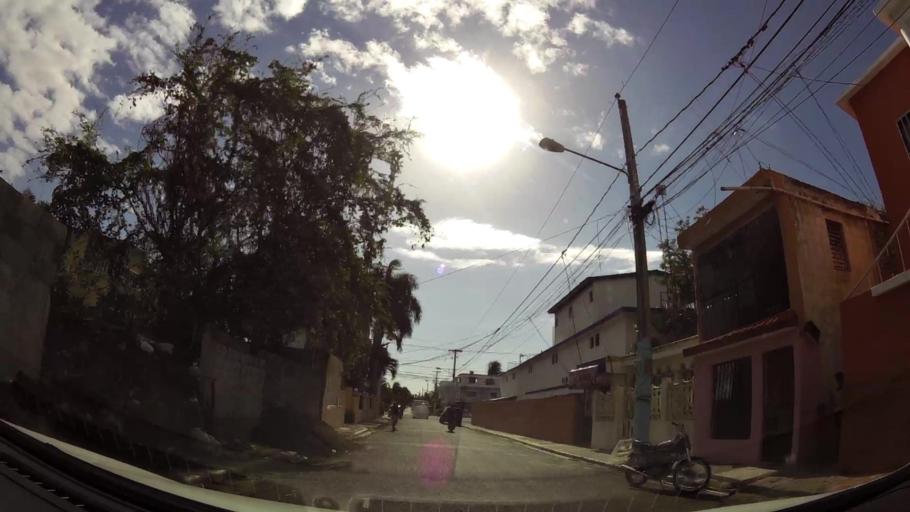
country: DO
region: Santo Domingo
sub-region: Santo Domingo
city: Boca Chica
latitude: 18.4531
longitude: -69.6091
